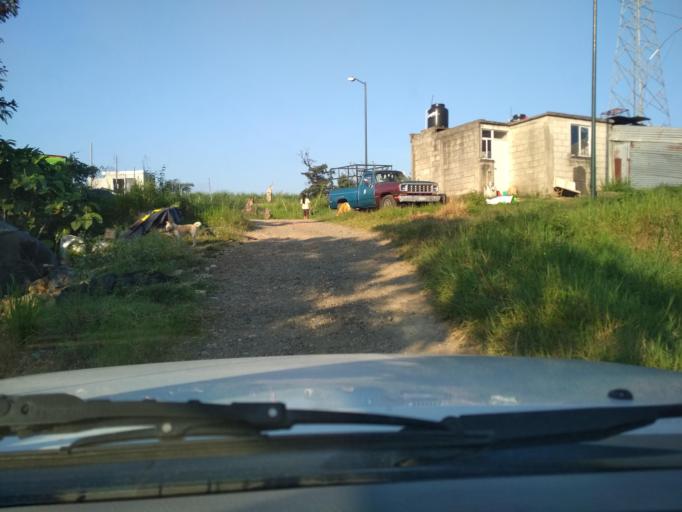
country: MX
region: Veracruz
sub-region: Cordoba
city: Veinte de Noviembre
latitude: 18.8695
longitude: -96.9385
